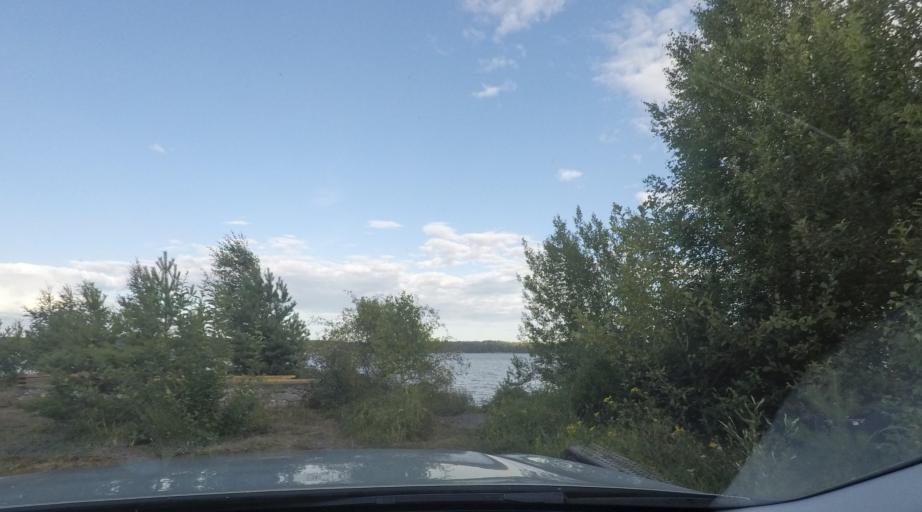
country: SE
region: Stockholm
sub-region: Nynashamns Kommun
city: Osmo
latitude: 58.9740
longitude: 17.7193
